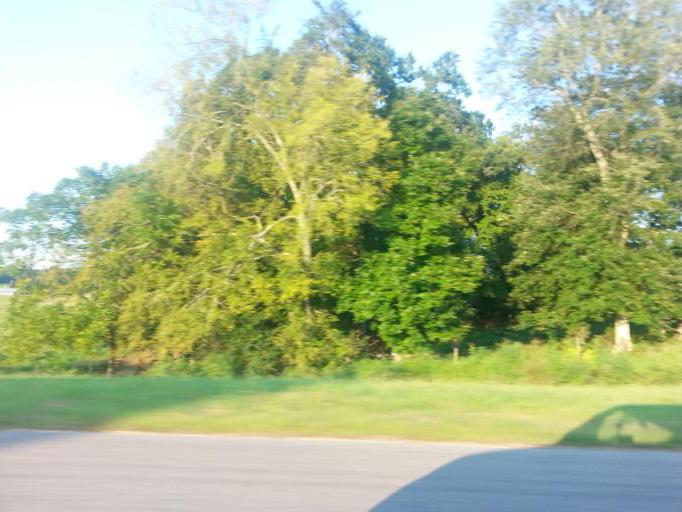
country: US
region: Tennessee
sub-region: McMinn County
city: Athens
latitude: 35.5458
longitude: -84.6630
